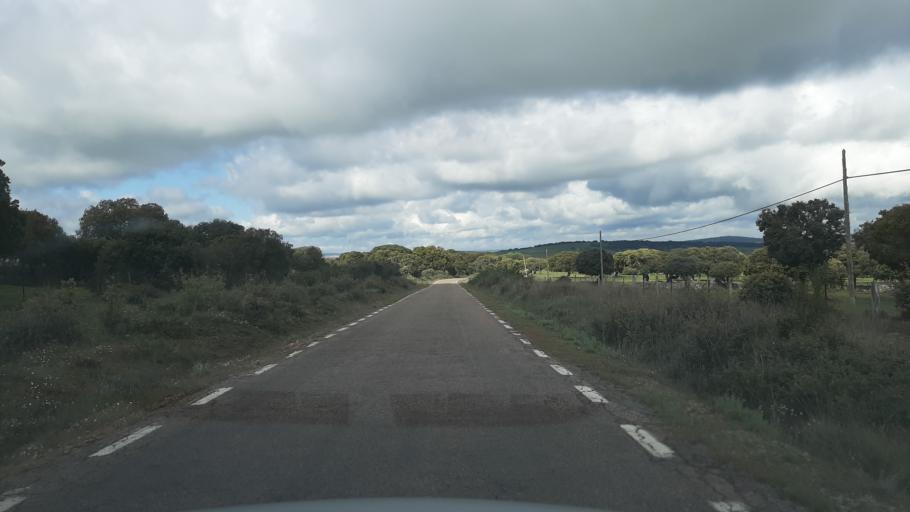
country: ES
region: Castille and Leon
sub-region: Provincia de Salamanca
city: Narros de Matalayegua
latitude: 40.7034
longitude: -5.9077
